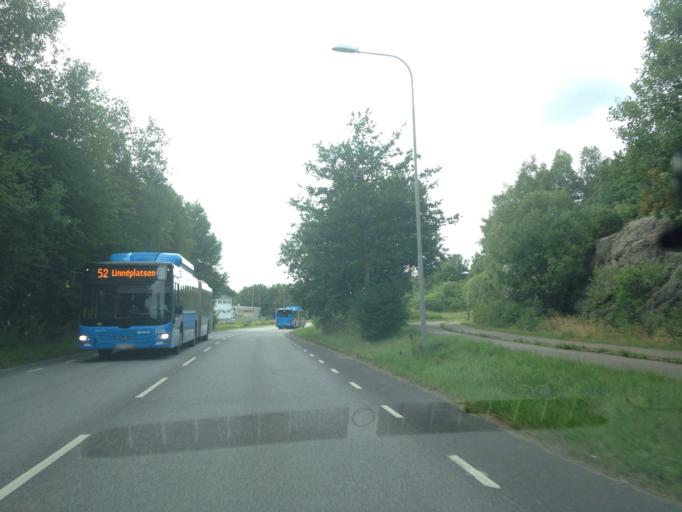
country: SE
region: Vaestra Goetaland
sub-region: Goteborg
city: Goeteborg
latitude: 57.7405
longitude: 11.9545
